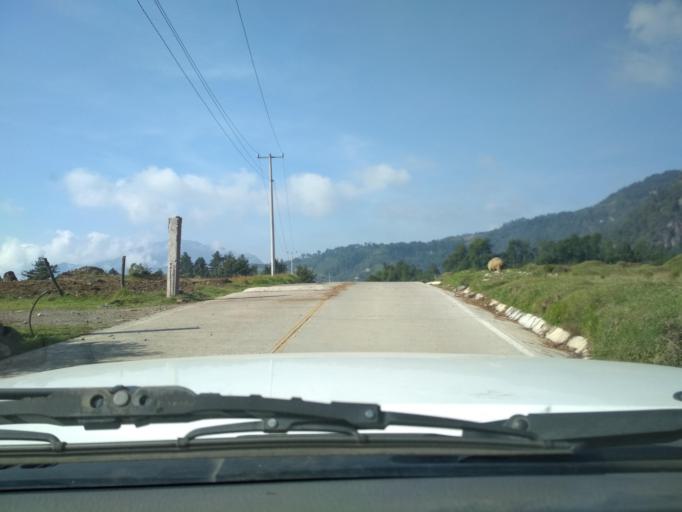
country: MX
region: Veracruz
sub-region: La Perla
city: Chilapa
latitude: 19.0031
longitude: -97.1820
